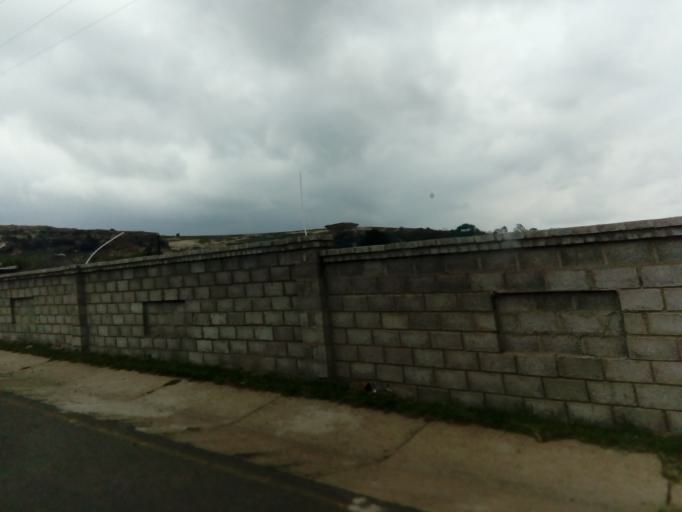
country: LS
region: Leribe
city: Leribe
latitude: -29.0301
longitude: 28.0243
